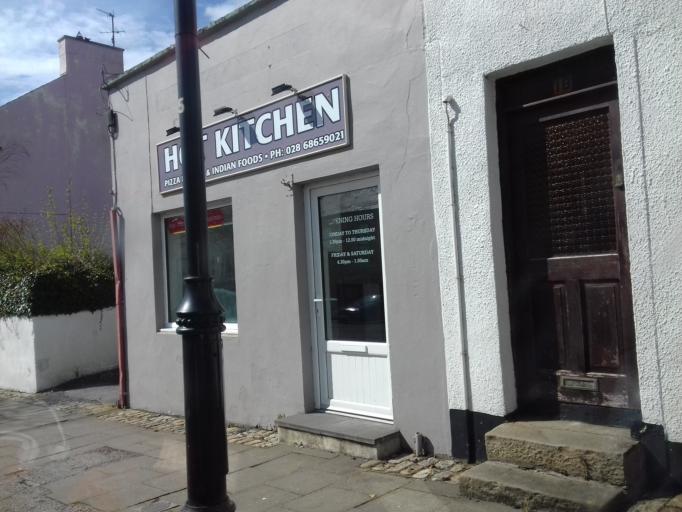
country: IE
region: Ulster
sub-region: County Donegal
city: Ballyshannon
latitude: 54.4800
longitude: -8.0926
